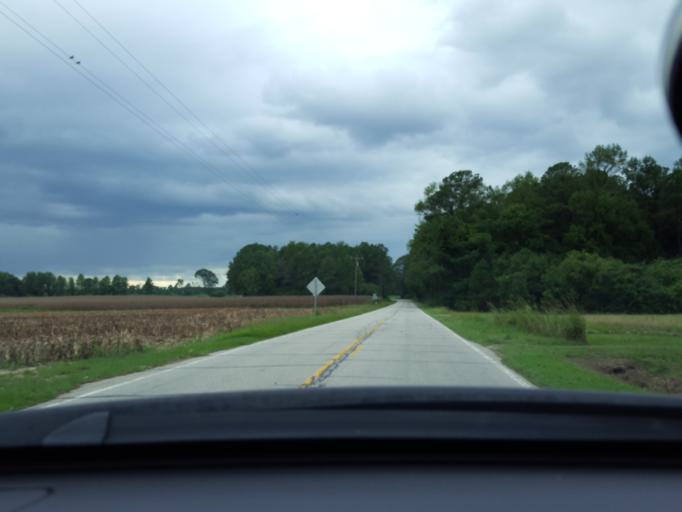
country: US
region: North Carolina
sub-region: Duplin County
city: Rose Hill
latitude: 34.8012
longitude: -78.2155
